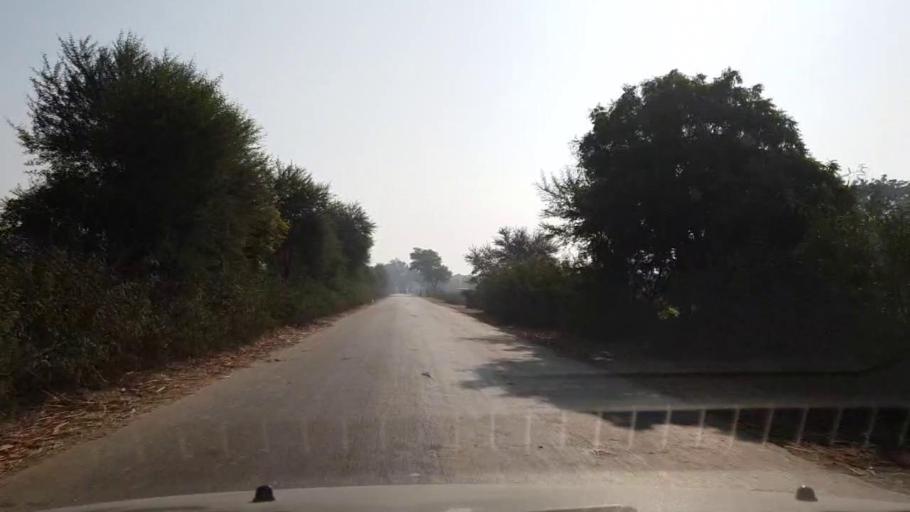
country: PK
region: Sindh
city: Matiari
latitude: 25.5718
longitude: 68.5120
